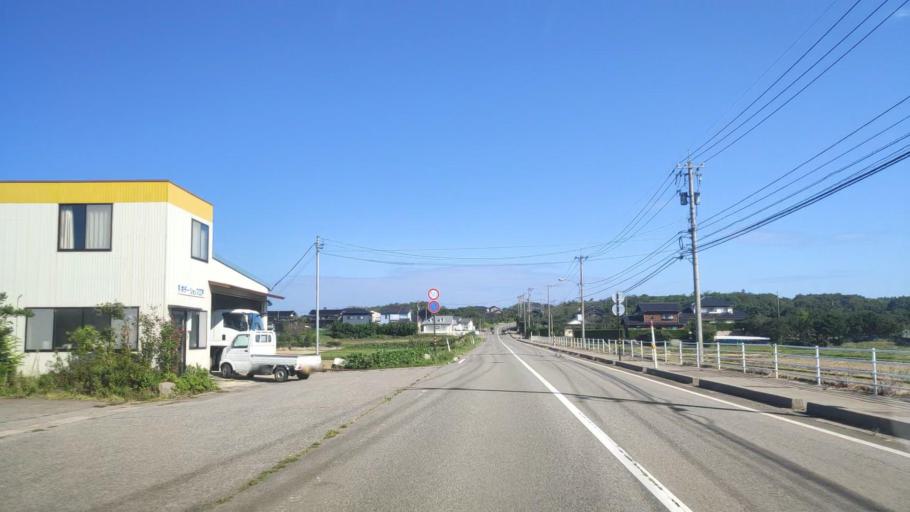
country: JP
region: Ishikawa
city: Hakui
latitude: 36.9827
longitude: 136.7761
